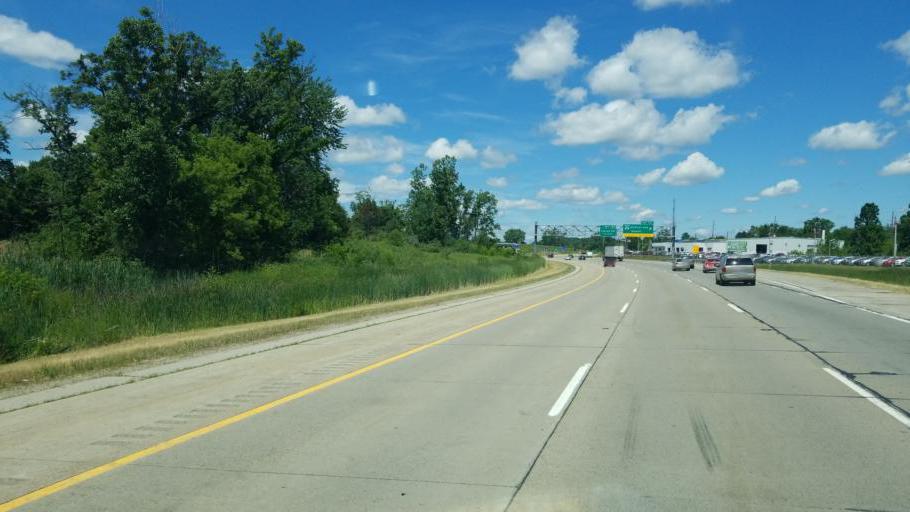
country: US
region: Michigan
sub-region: Livingston County
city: Howell
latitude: 42.5768
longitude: -83.8519
